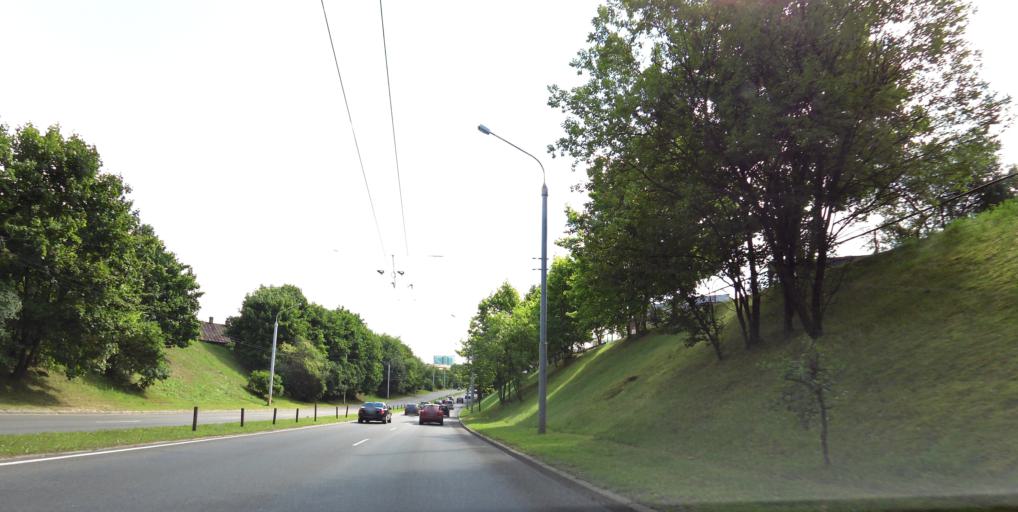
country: LT
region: Vilnius County
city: Seskine
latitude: 54.6996
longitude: 25.2488
